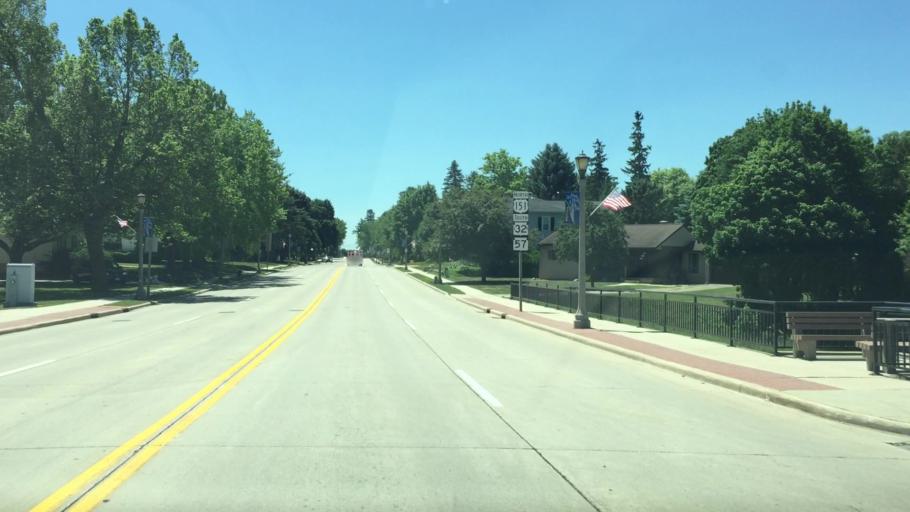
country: US
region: Wisconsin
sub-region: Calumet County
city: Chilton
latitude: 44.0279
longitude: -88.1629
